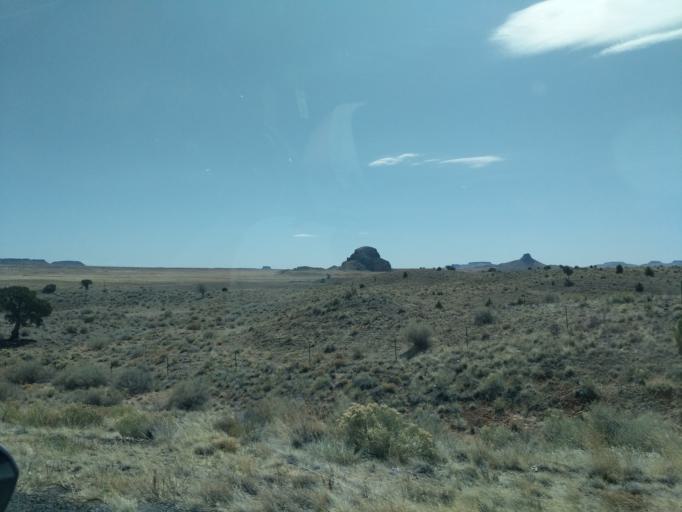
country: US
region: Arizona
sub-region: Navajo County
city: Dilkon
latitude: 35.3944
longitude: -110.0805
